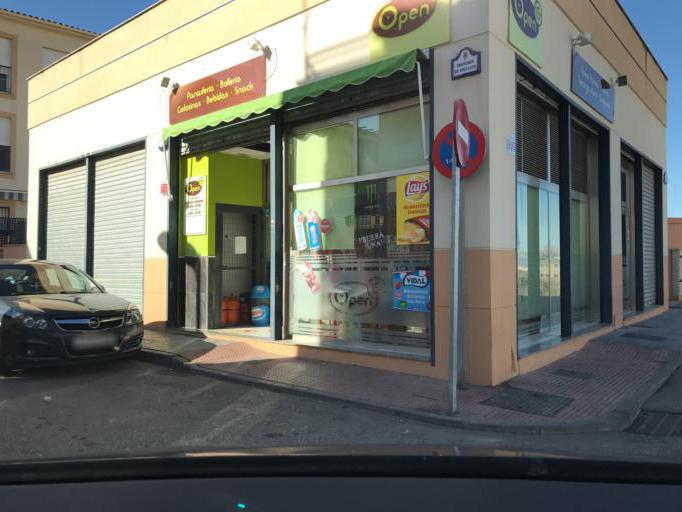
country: ES
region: Andalusia
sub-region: Provincia de Granada
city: Cullar-Vega
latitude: 37.1395
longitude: -3.6641
